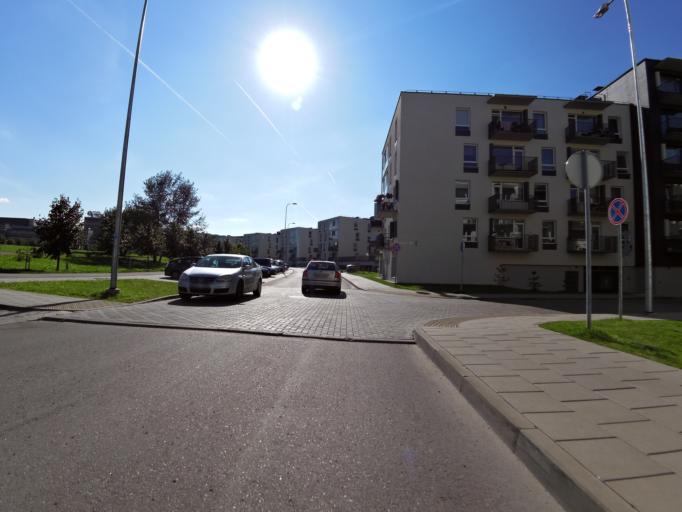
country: LT
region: Vilnius County
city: Seskine
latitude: 54.7191
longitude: 25.2788
